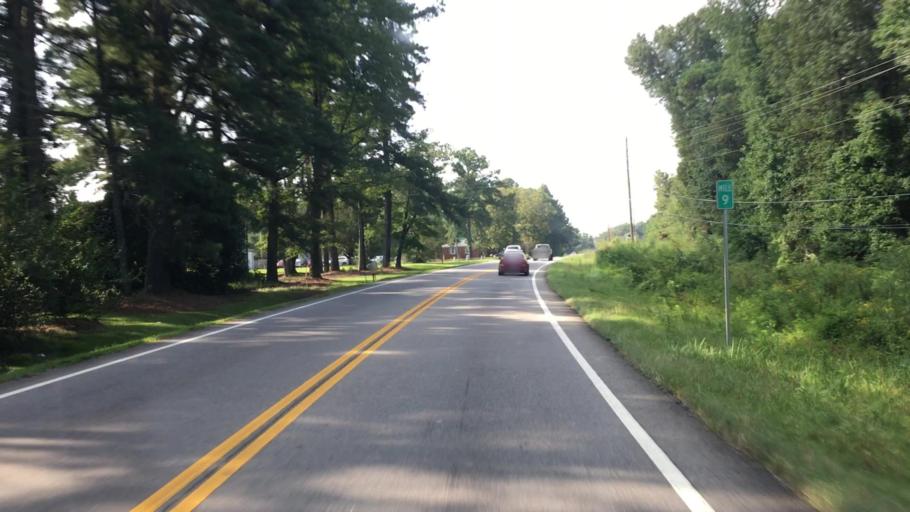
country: US
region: Georgia
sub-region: Walton County
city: Monroe
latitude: 33.7356
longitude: -83.7015
